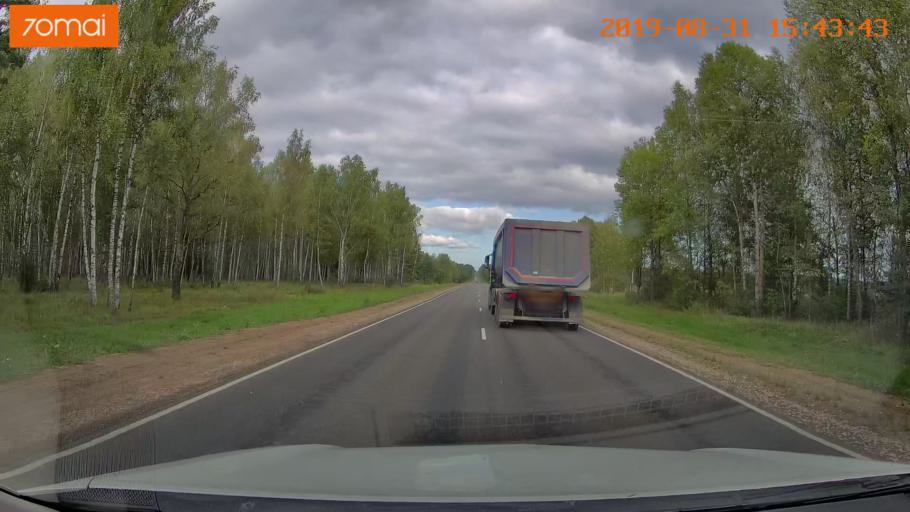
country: RU
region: Kaluga
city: Mosal'sk
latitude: 54.6543
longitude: 34.9154
